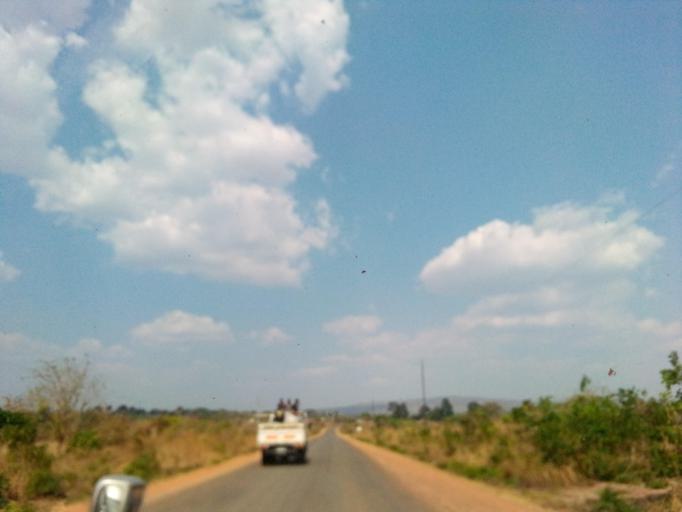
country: ZM
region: Northern
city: Mpika
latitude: -11.8330
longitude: 31.4159
